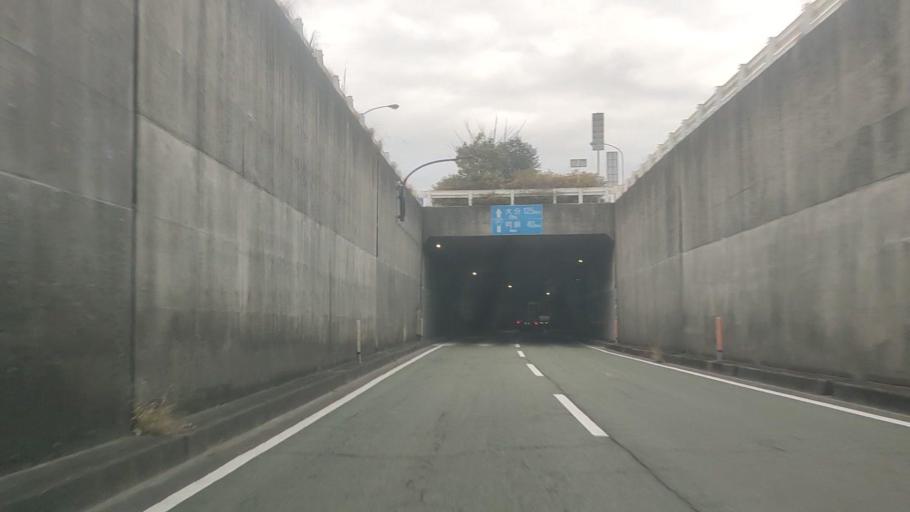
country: JP
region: Kumamoto
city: Ozu
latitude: 32.8528
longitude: 130.7833
